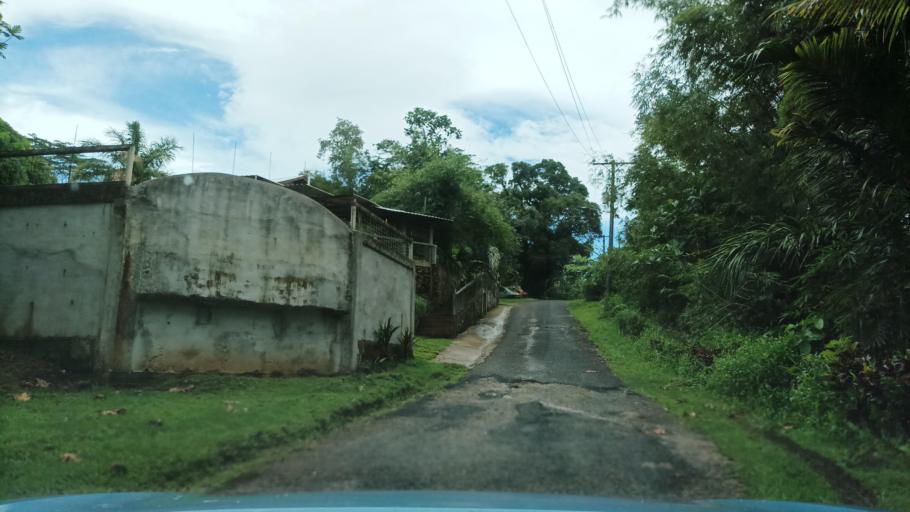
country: FM
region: Pohnpei
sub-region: Sokehs Municipality
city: Palikir - National Government Center
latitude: 6.8328
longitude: 158.1703
